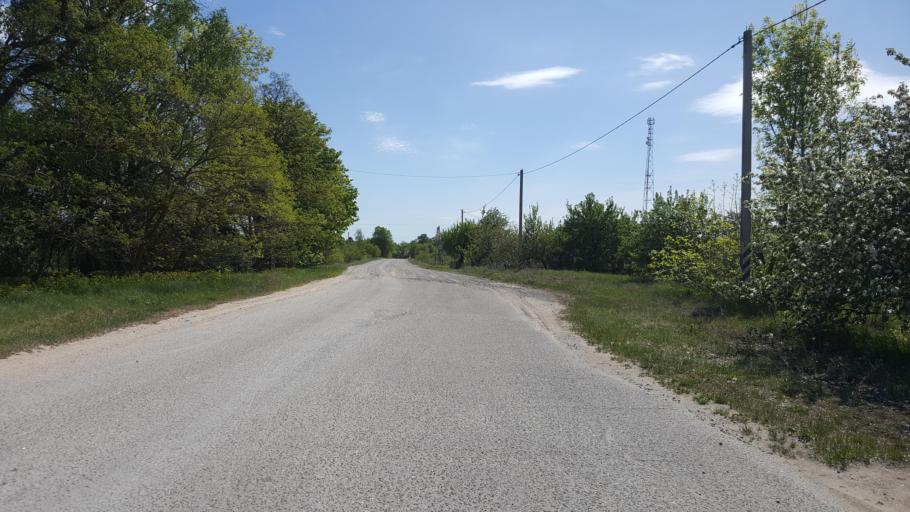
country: BY
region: Brest
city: Zhabinka
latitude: 52.3597
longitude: 24.1566
